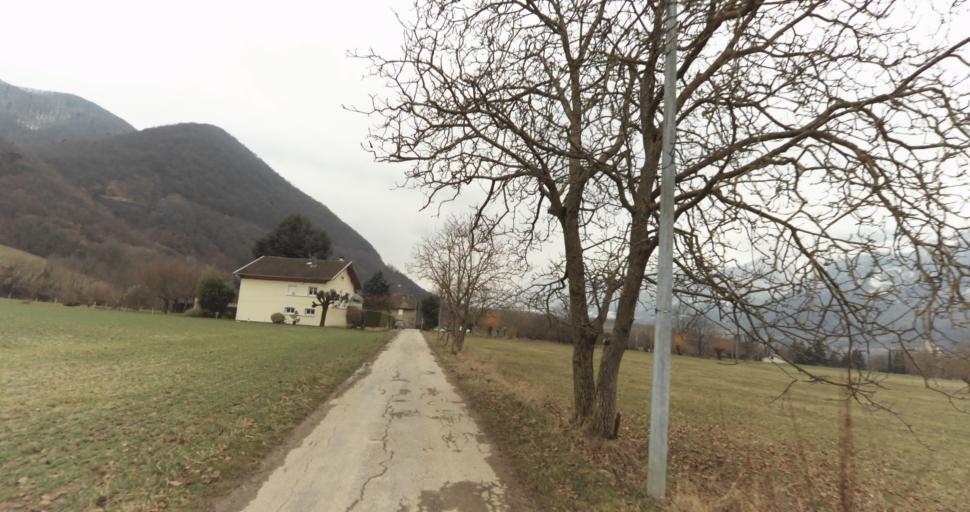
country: FR
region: Rhone-Alpes
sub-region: Departement de l'Isere
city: Vif
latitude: 45.0425
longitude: 5.6743
